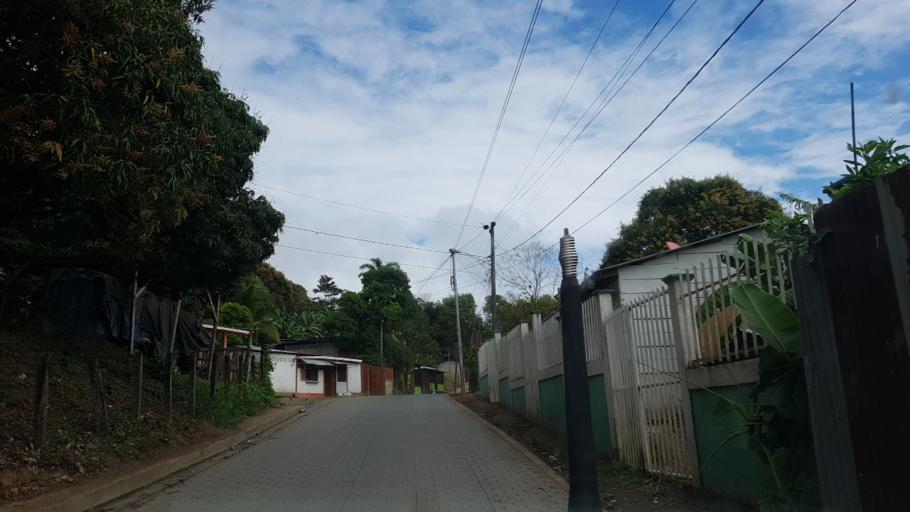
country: NI
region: Atlantico Norte (RAAN)
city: Siuna
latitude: 13.7389
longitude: -84.7818
